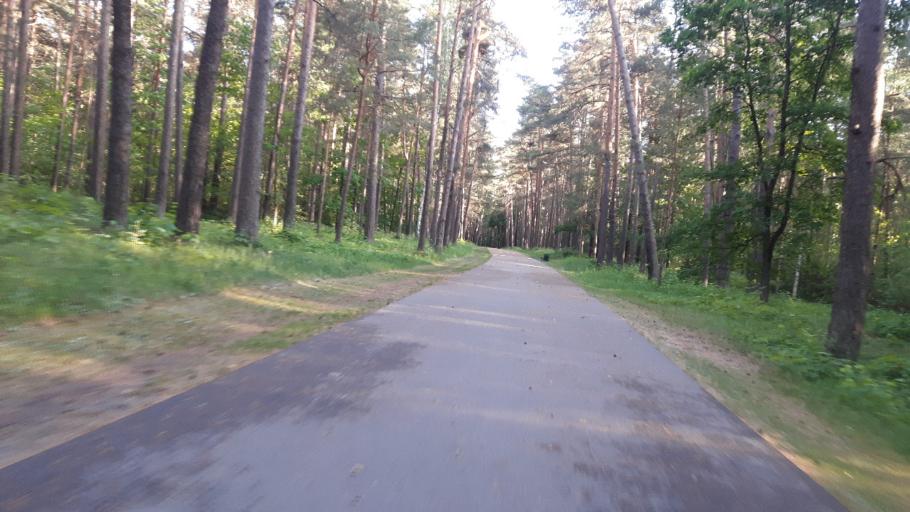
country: LV
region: Riga
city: Jaunciems
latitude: 57.0069
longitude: 24.1459
